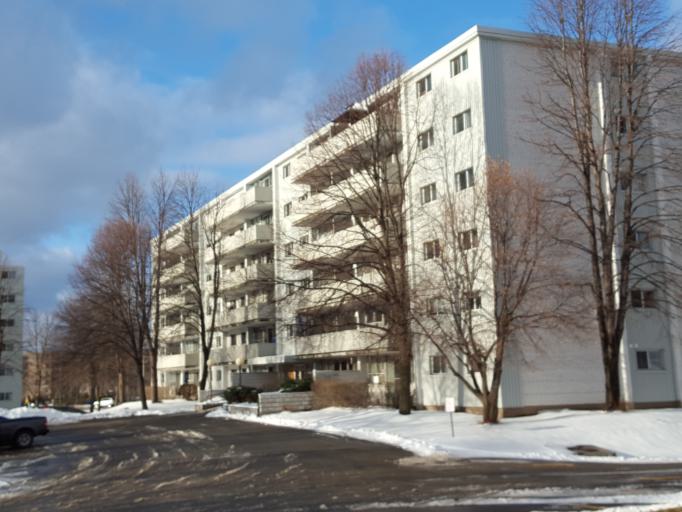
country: CA
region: Ontario
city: Kingston
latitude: 44.2377
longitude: -76.5339
